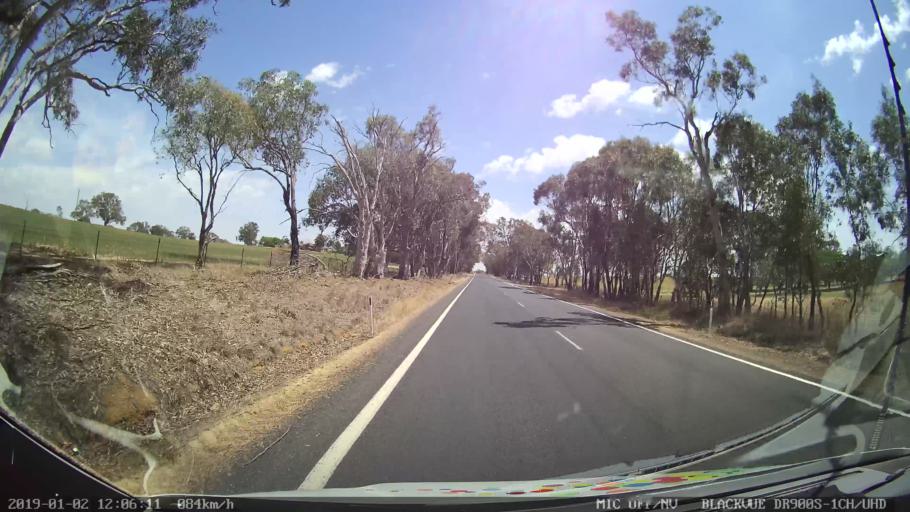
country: AU
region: New South Wales
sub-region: Young
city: Young
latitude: -34.5058
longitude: 148.2966
